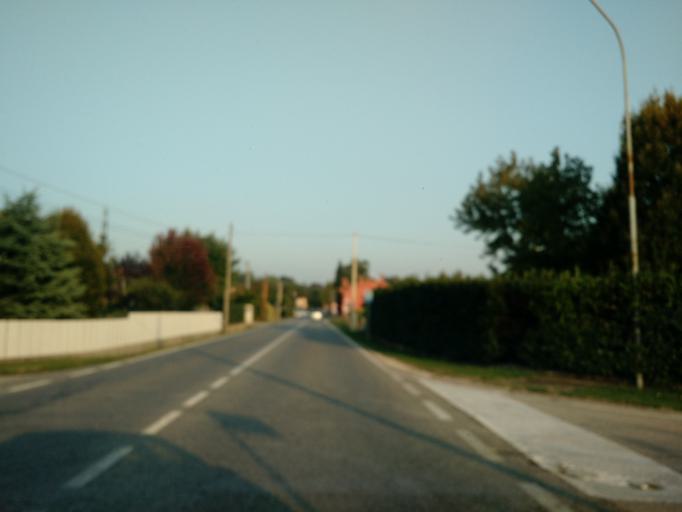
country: IT
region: Veneto
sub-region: Provincia di Vicenza
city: Sarcedo
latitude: 45.7013
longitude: 11.5173
